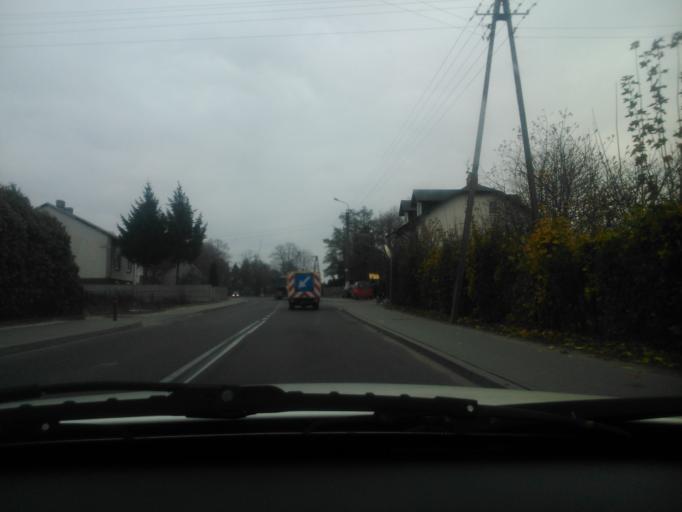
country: PL
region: Masovian Voivodeship
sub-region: Powiat zurominski
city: Zuromin
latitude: 53.0917
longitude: 19.9720
